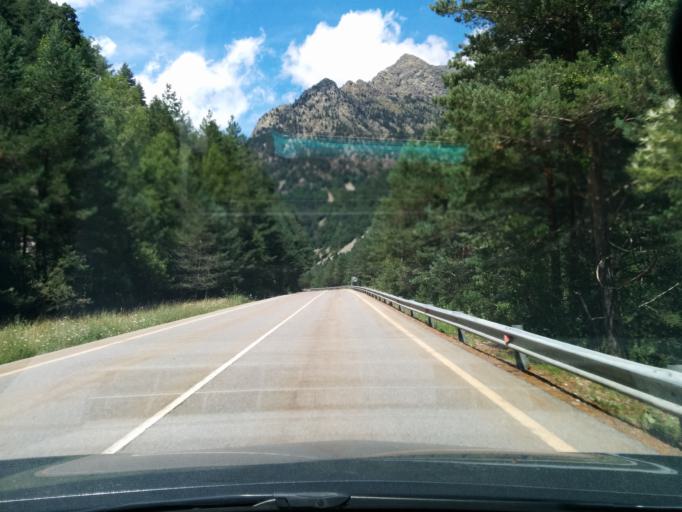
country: ES
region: Aragon
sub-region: Provincia de Huesca
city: Bielsa
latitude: 42.6800
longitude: 0.2133
